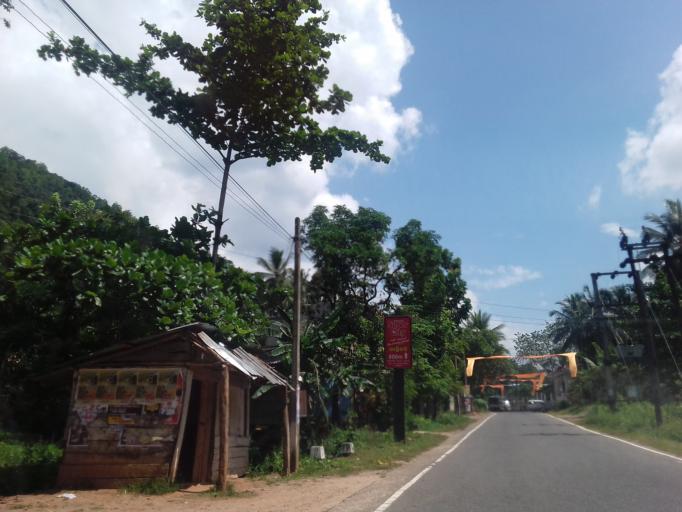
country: LK
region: Central
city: Hatton
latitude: 6.9976
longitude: 80.3533
